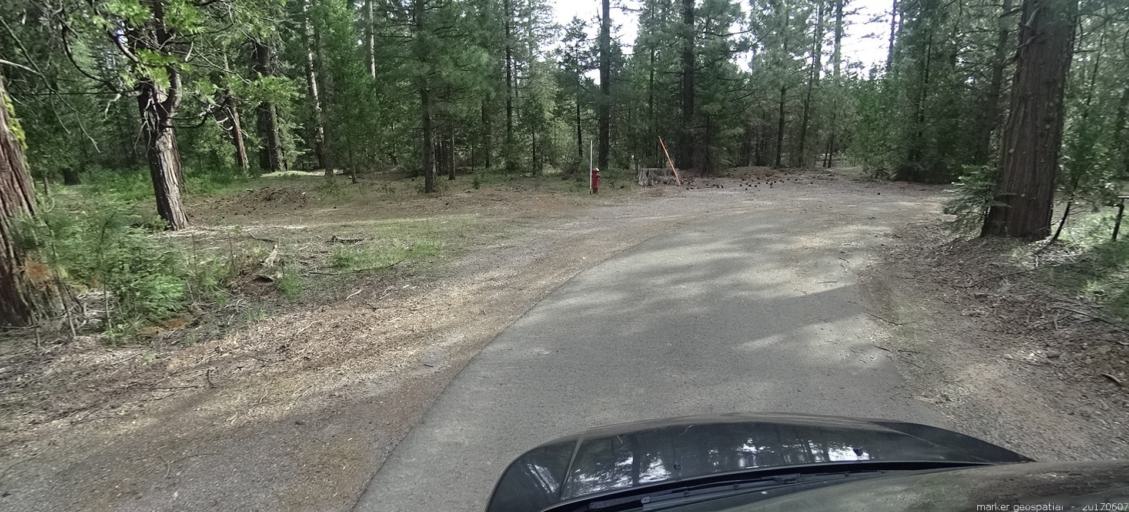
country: US
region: California
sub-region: Shasta County
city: Burney
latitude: 41.1998
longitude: -121.6874
